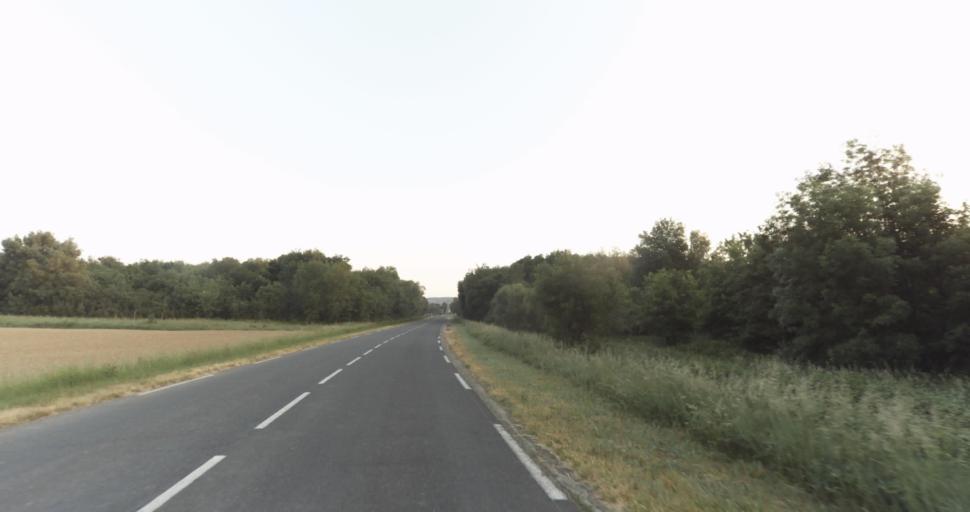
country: FR
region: Midi-Pyrenees
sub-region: Departement du Gers
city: Pujaudran
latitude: 43.6429
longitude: 1.1408
